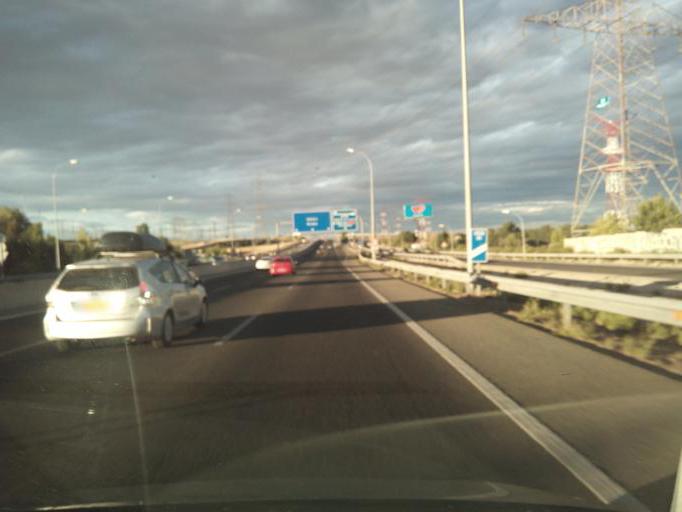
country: ES
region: Madrid
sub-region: Provincia de Madrid
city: San Sebastian de los Reyes
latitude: 40.5578
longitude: -3.6011
